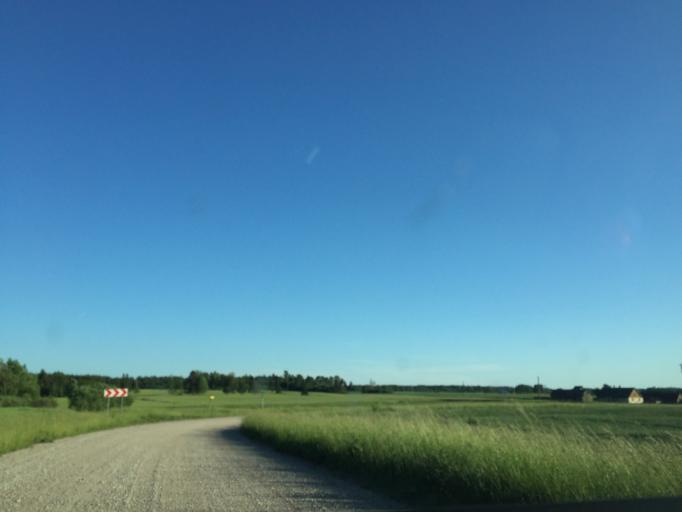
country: LV
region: Broceni
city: Broceni
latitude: 56.8650
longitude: 22.6057
